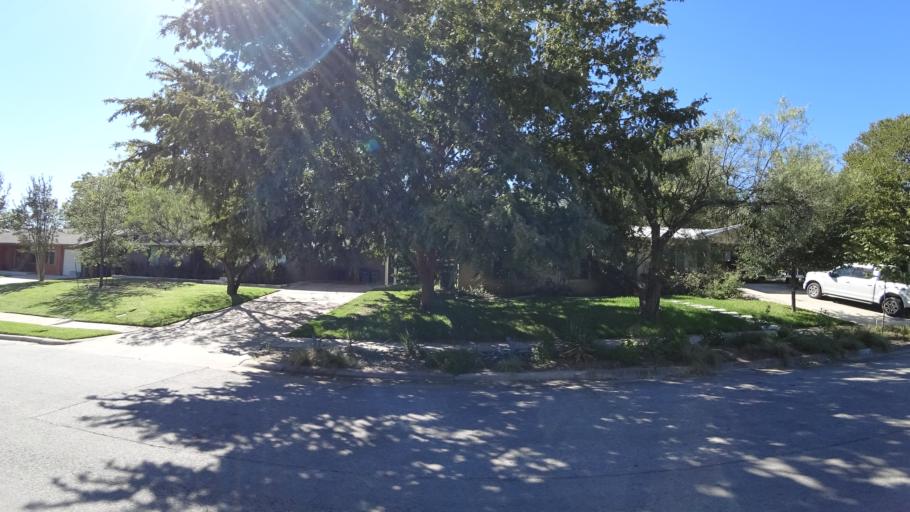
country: US
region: Texas
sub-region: Travis County
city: West Lake Hills
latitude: 30.3361
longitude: -97.7515
